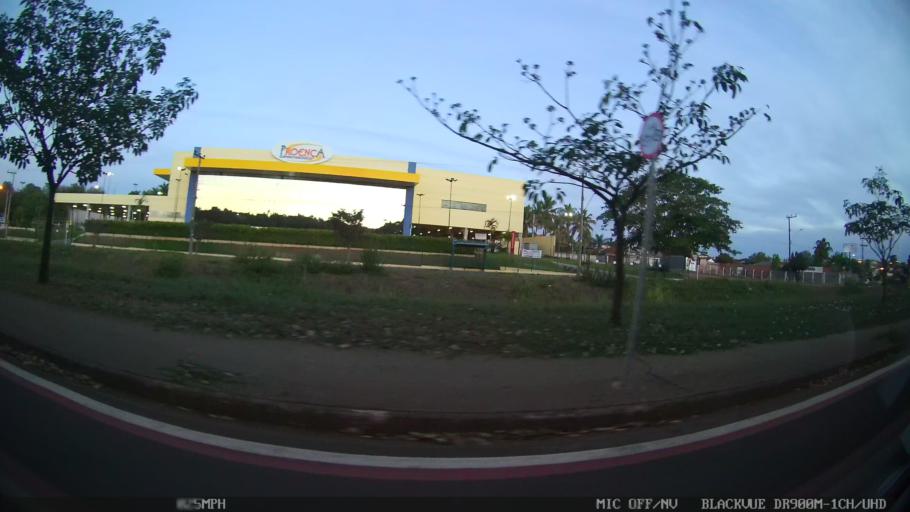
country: BR
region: Sao Paulo
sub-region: Catanduva
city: Catanduva
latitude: -21.1338
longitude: -48.9887
